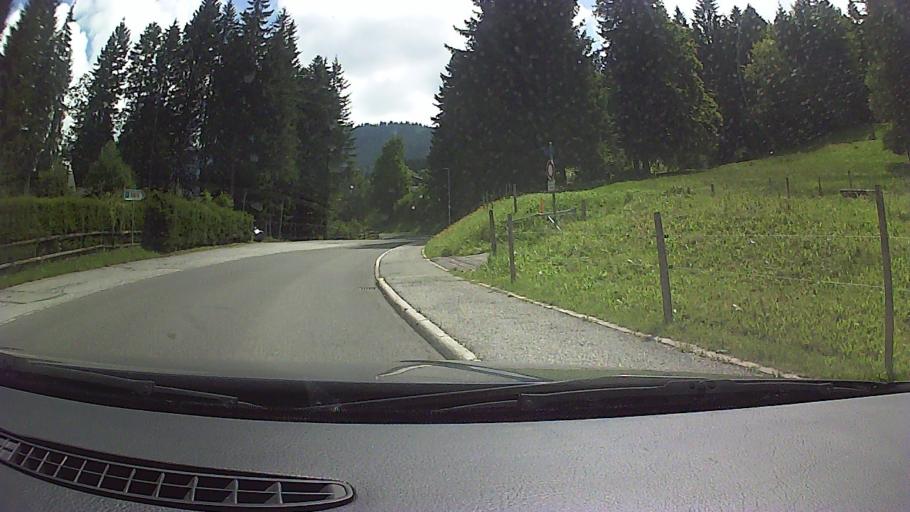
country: CH
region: Fribourg
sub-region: Veveyse District
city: Chatel-Saint-Denis
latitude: 46.5211
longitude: 6.9517
